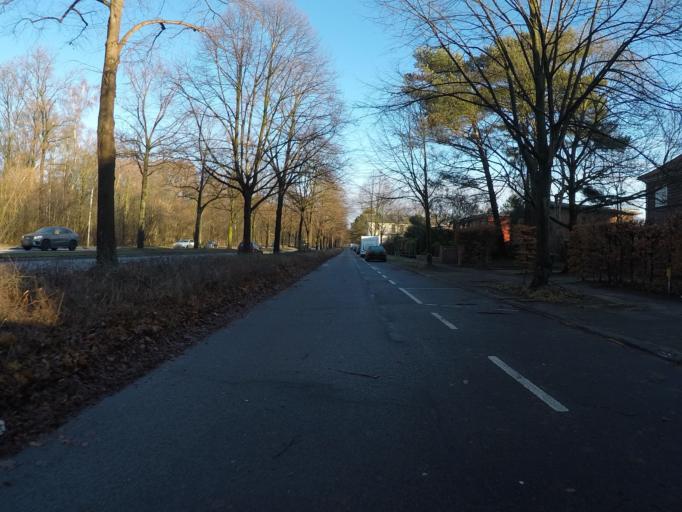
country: DE
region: Hamburg
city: Winterhude
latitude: 53.6076
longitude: 9.9923
